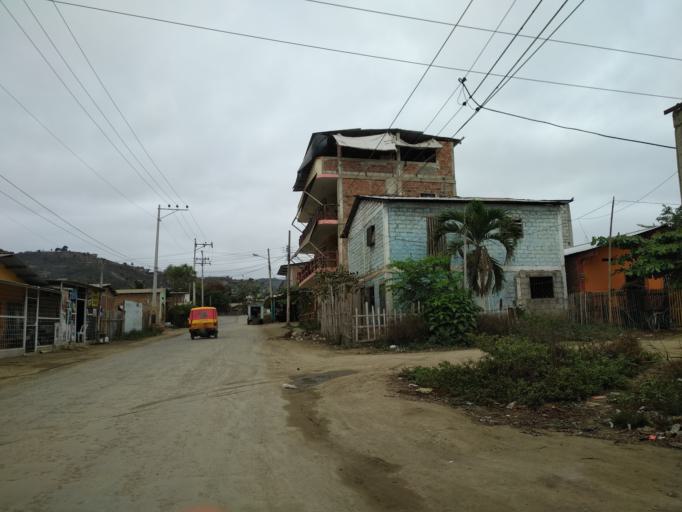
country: EC
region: Manabi
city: Jipijapa
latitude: -1.5530
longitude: -80.8087
